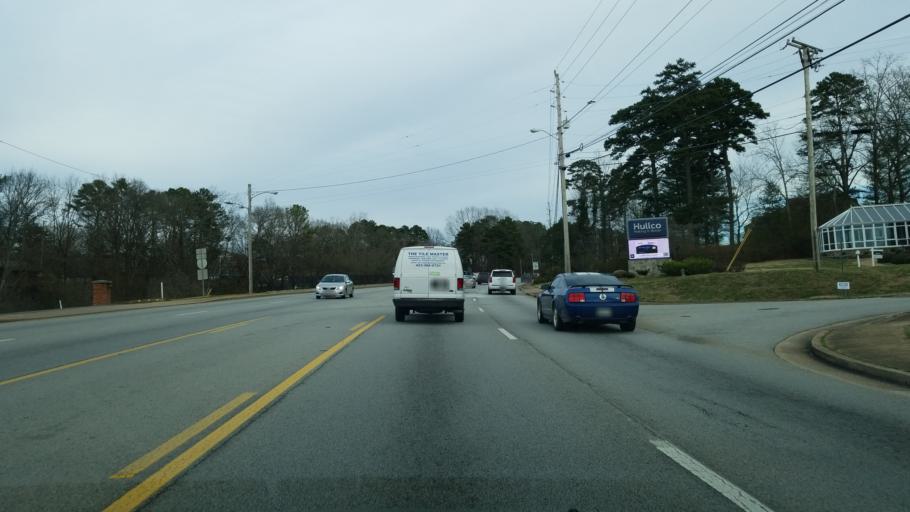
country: US
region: Tennessee
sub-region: Hamilton County
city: East Brainerd
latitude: 35.0181
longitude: -85.1722
